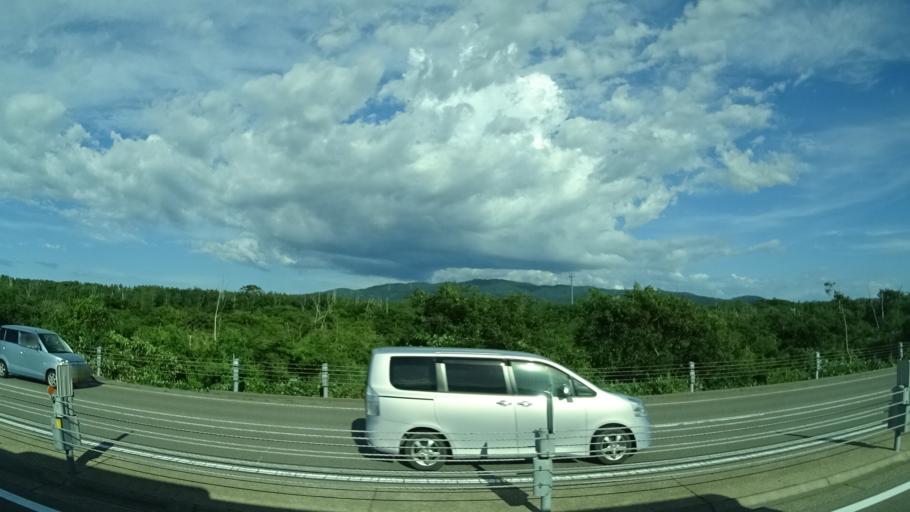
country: JP
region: Ishikawa
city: Hakui
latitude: 36.8090
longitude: 136.7373
